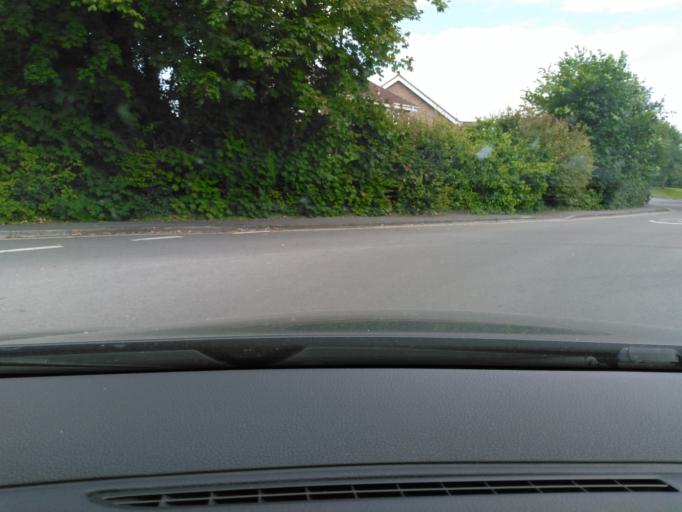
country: GB
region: England
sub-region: Hampshire
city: Andover
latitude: 51.2036
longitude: -1.5001
